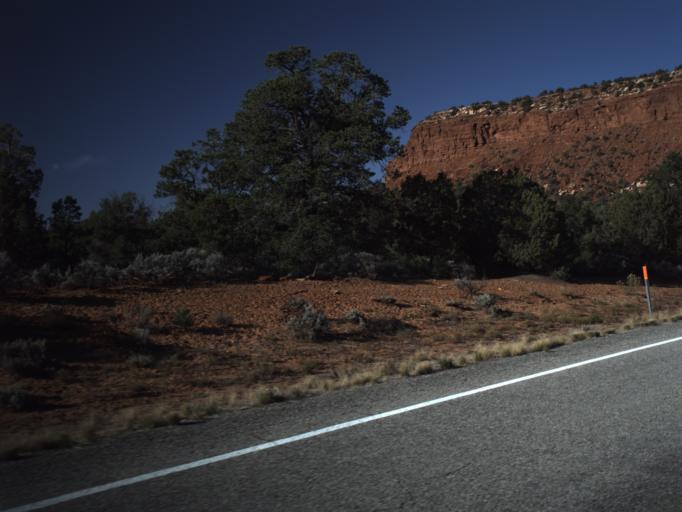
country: US
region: Utah
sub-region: San Juan County
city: Blanding
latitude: 37.5625
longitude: -110.0233
